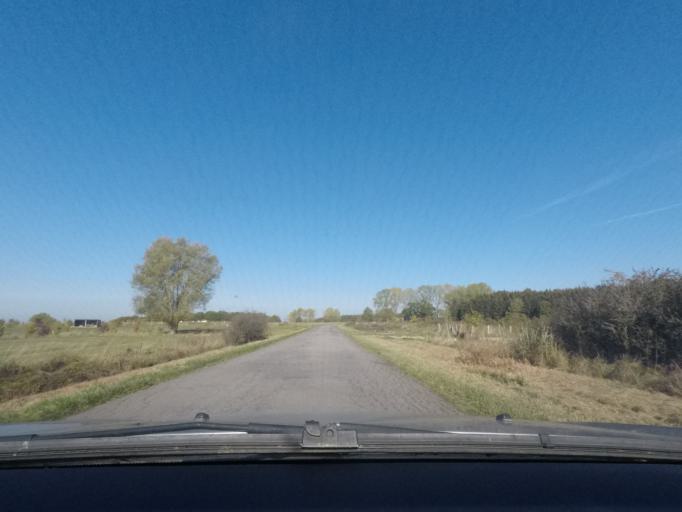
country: BE
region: Wallonia
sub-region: Province du Luxembourg
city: Etalle
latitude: 49.6965
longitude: 5.5721
